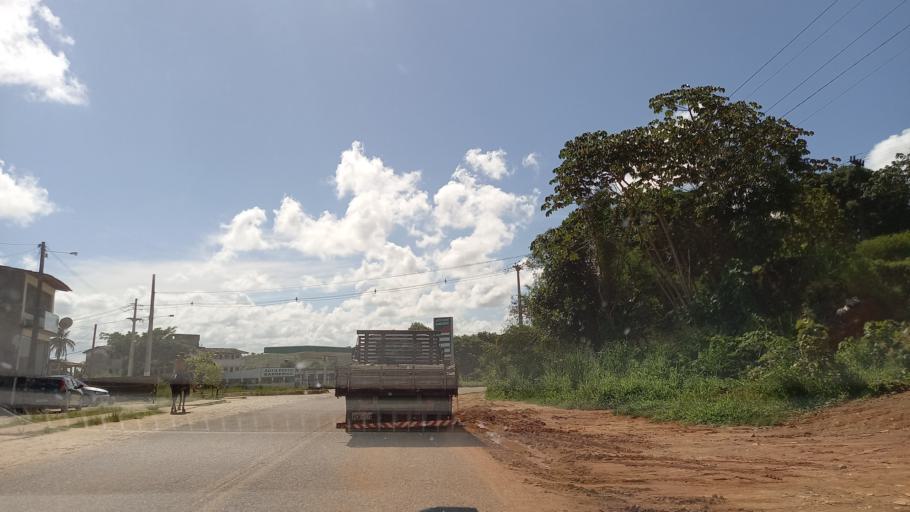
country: BR
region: Pernambuco
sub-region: Barreiros
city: Barreiros
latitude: -8.8012
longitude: -35.1896
